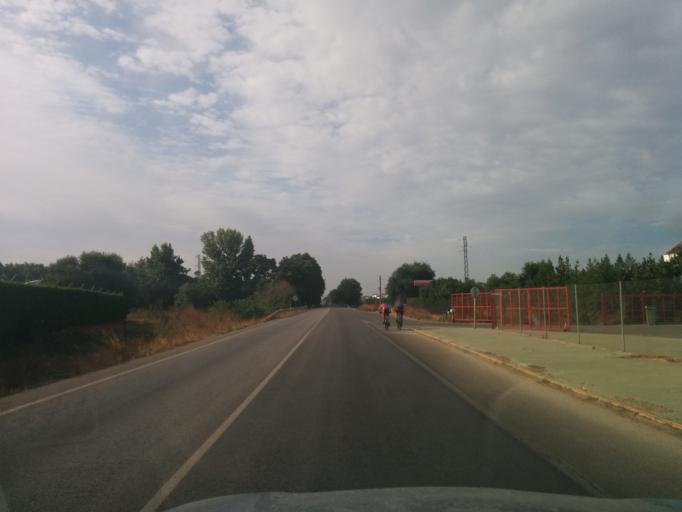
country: ES
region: Andalusia
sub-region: Provincia de Sevilla
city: La Algaba
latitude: 37.4783
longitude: -6.0088
